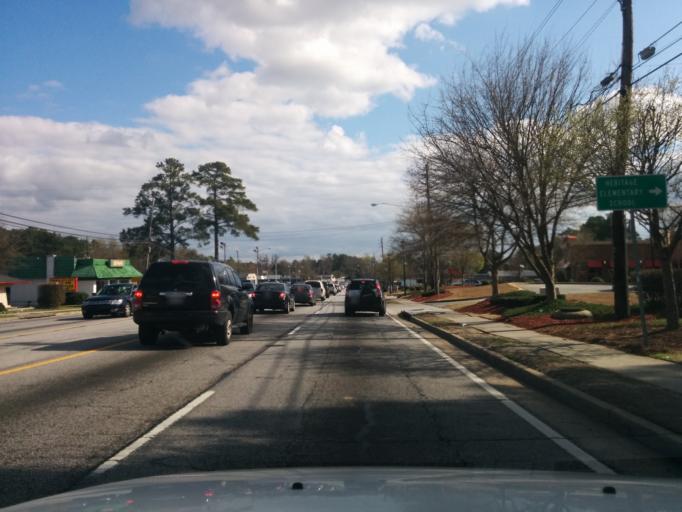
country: US
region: Georgia
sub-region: Fulton County
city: College Park
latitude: 33.6129
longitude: -84.4723
